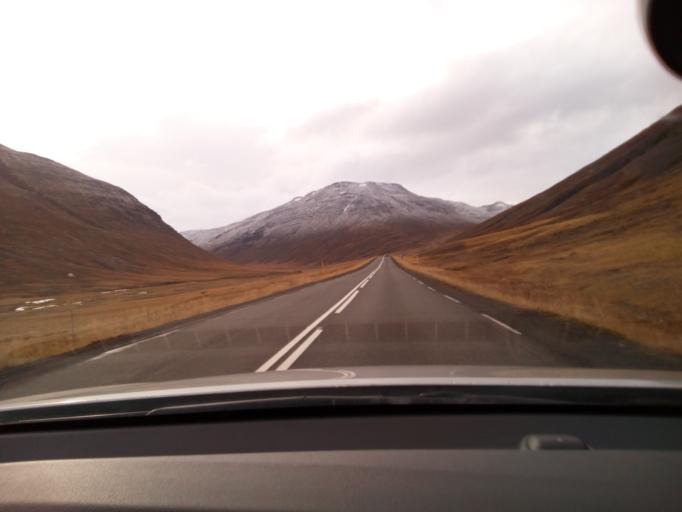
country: IS
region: Northeast
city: Dalvik
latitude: 65.4889
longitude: -18.6442
